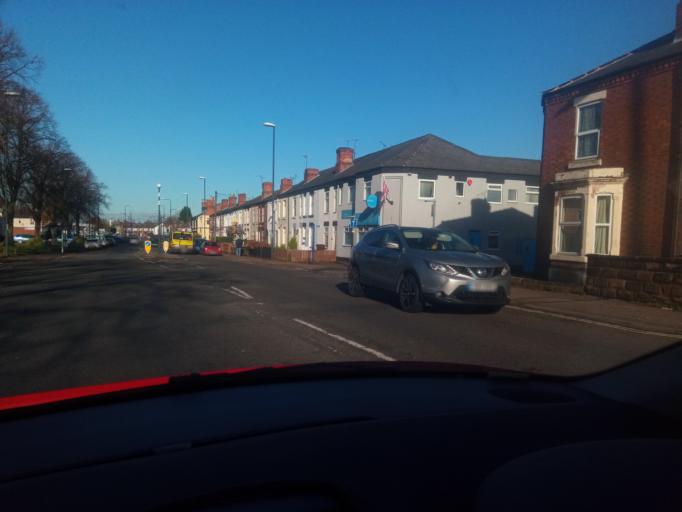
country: GB
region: England
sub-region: Derby
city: Derby
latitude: 52.8881
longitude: -1.4506
